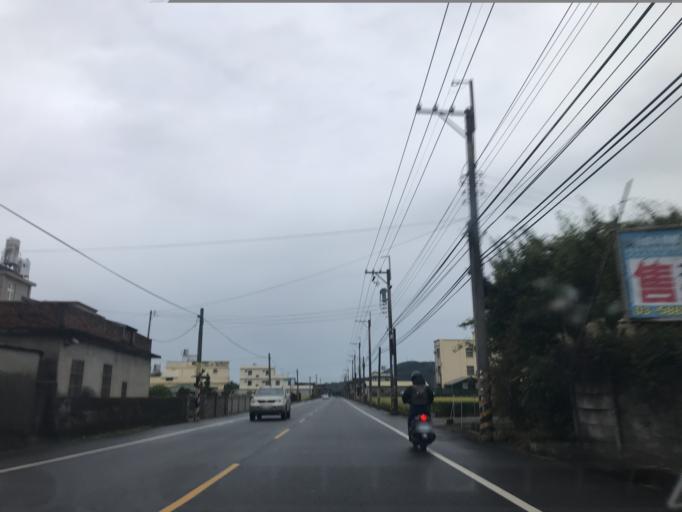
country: TW
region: Taiwan
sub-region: Hsinchu
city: Zhubei
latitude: 24.8406
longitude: 121.1171
